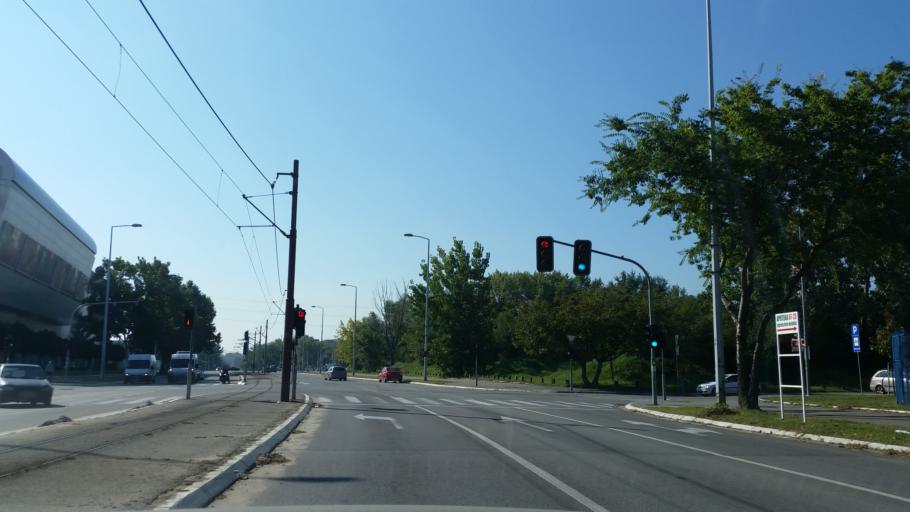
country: RS
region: Central Serbia
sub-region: Belgrade
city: Novi Beograd
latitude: 44.8067
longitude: 20.4036
